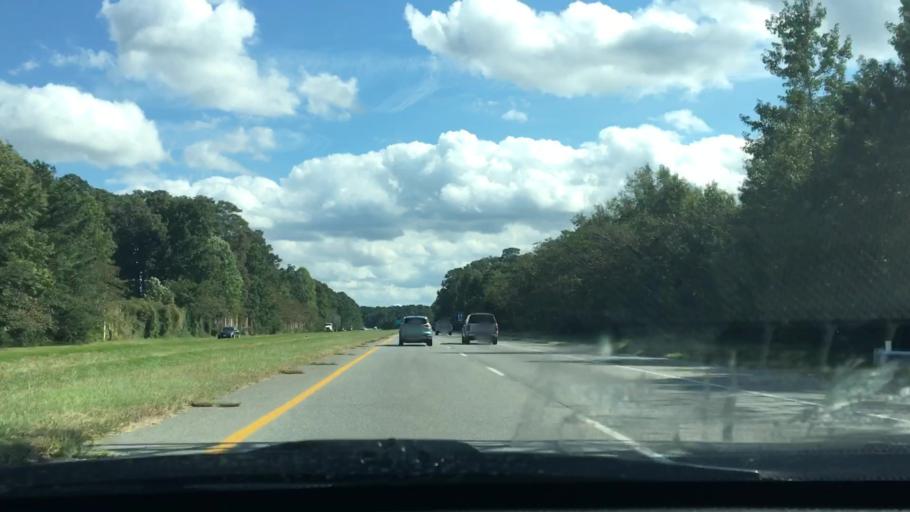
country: US
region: Virginia
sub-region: City of Chesapeake
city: Chesapeake
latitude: 36.7425
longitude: -76.2533
